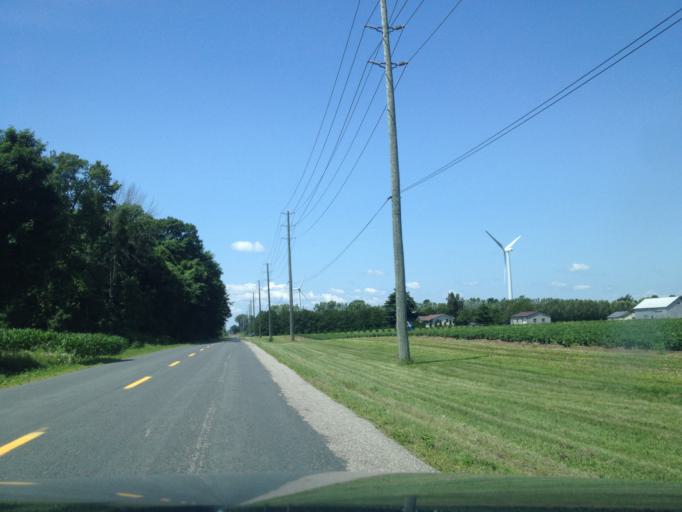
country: CA
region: Ontario
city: Aylmer
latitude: 42.6397
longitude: -80.7268
